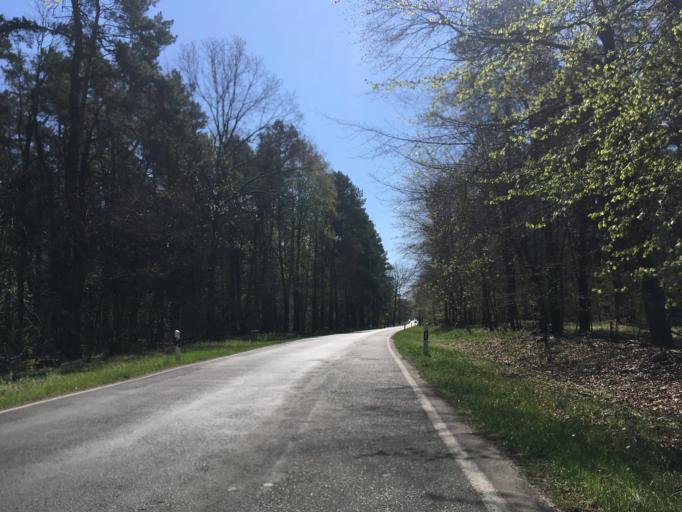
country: DE
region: Brandenburg
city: Bernau bei Berlin
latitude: 52.7132
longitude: 13.5787
